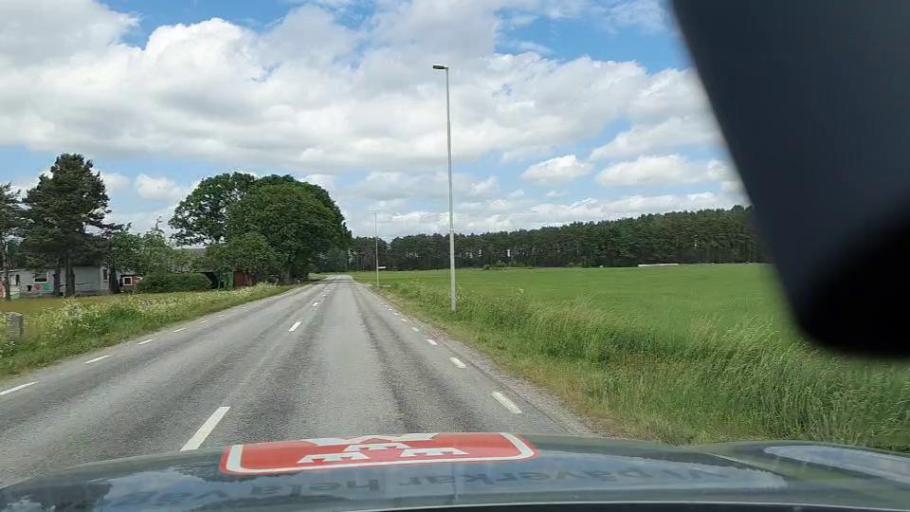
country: SE
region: Blekinge
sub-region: Karlshamns Kommun
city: Morrum
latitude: 56.0871
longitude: 14.7051
